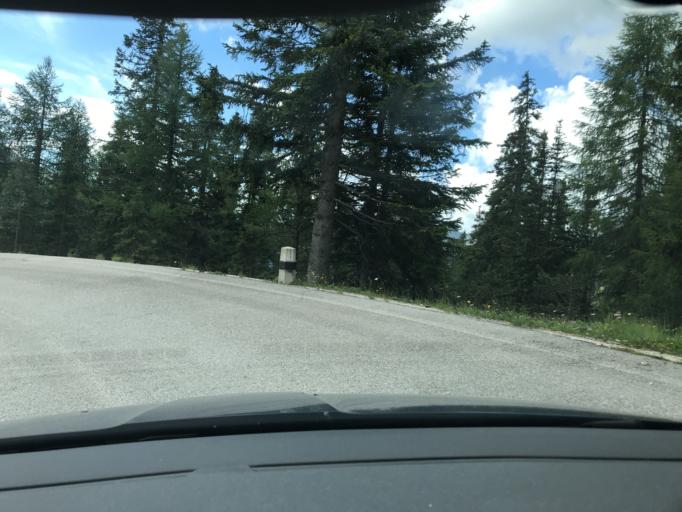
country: IT
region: Veneto
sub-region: Provincia di Belluno
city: Livinallongo del Col di Lana
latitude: 46.5133
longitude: 11.9958
